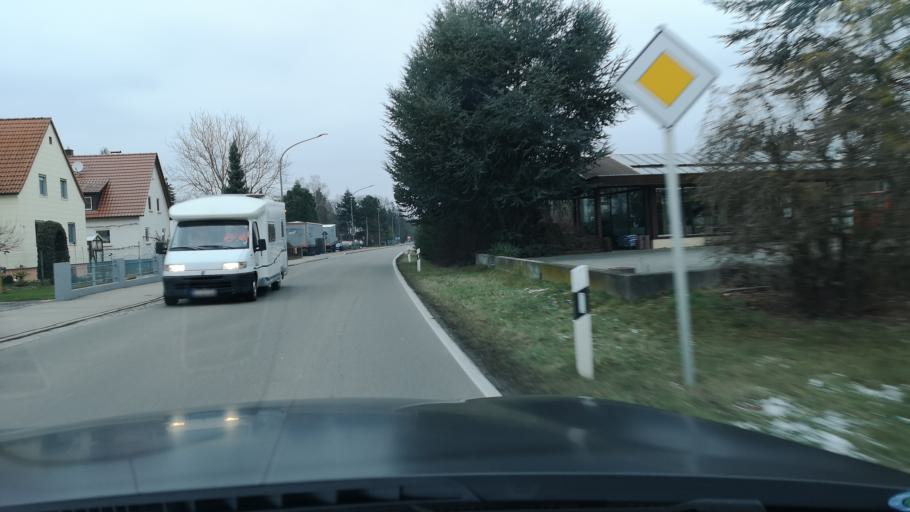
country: DE
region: Bavaria
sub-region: Swabia
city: Leipheim
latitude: 48.4301
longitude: 10.1898
